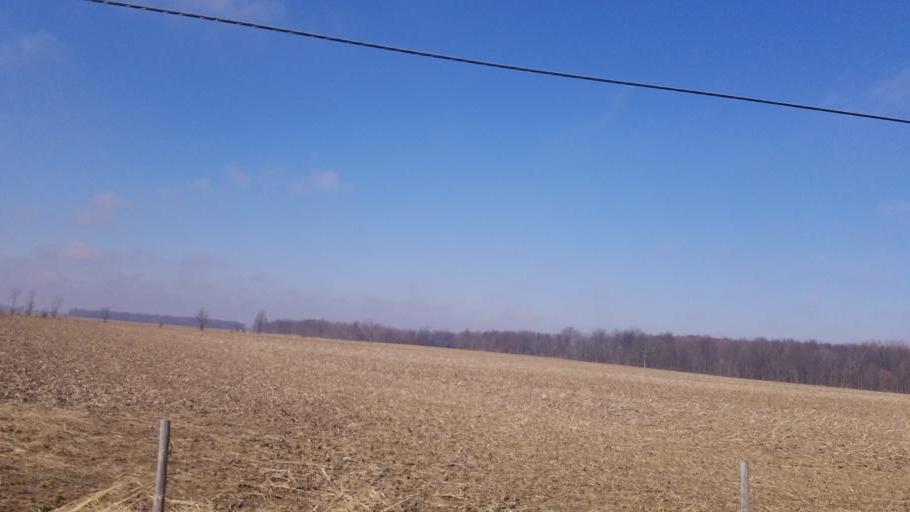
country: US
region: Ohio
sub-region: Huron County
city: Willard
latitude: 41.0113
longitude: -82.9141
